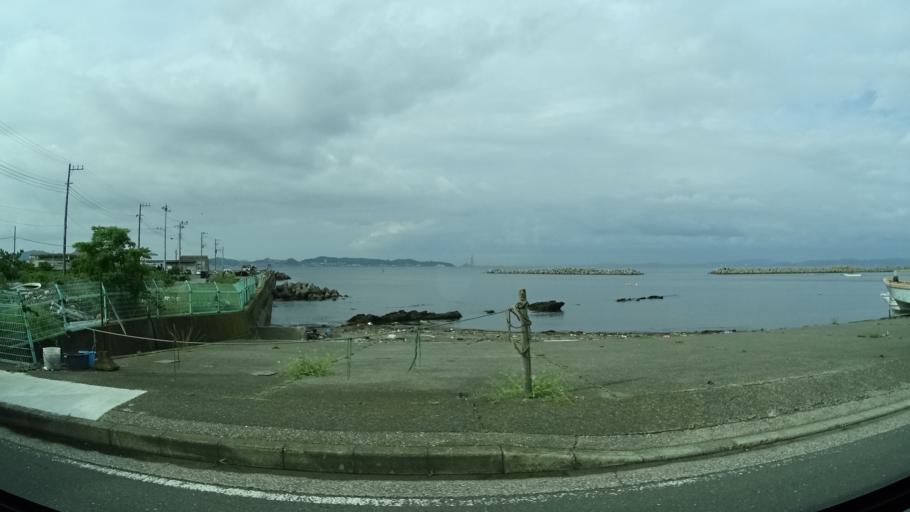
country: JP
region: Kanagawa
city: Miura
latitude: 35.1579
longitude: 139.6669
